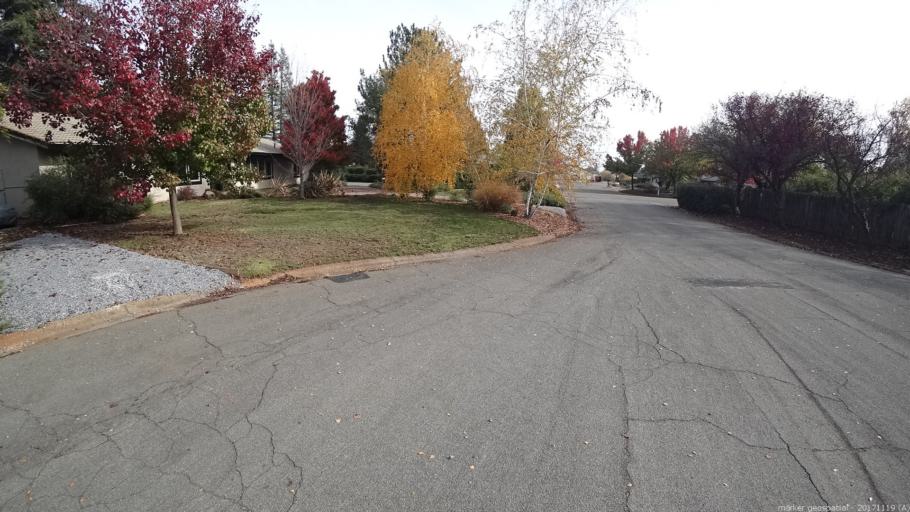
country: US
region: California
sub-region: Shasta County
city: Anderson
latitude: 40.4957
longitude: -122.3077
